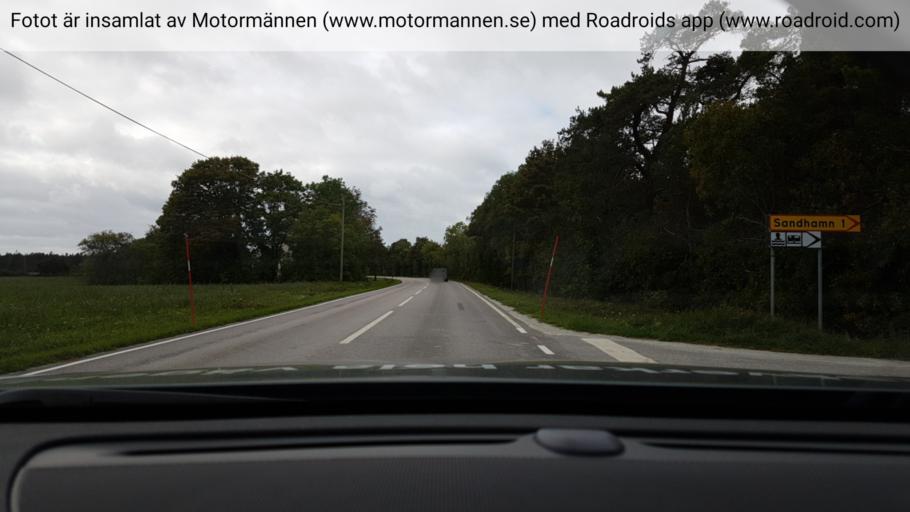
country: SE
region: Gotland
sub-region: Gotland
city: Klintehamn
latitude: 57.3177
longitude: 18.1794
